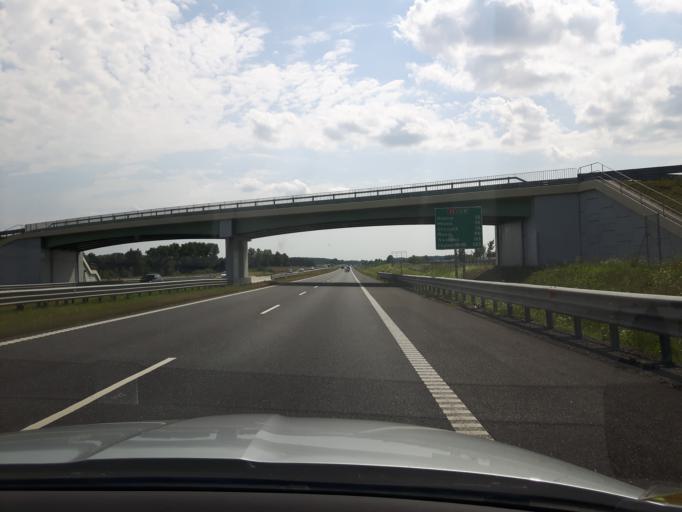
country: PL
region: Warmian-Masurian Voivodeship
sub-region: Powiat olsztynski
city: Olsztynek
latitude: 53.5672
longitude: 20.2625
